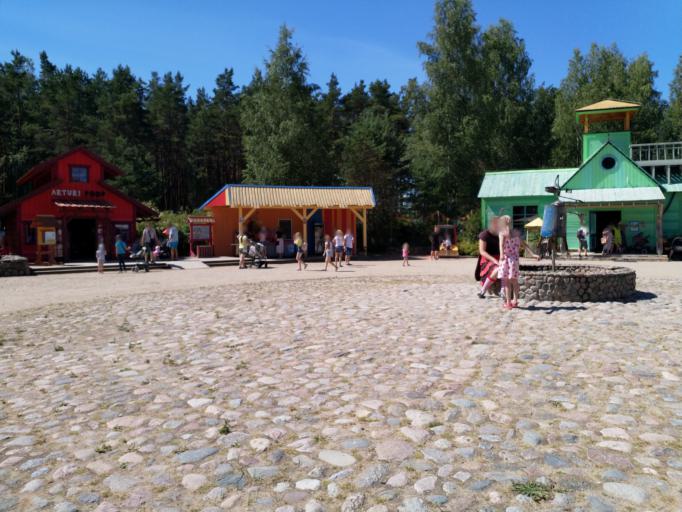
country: EE
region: Paernumaa
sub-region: Paikuse vald
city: Paikuse
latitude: 58.3011
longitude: 24.5885
